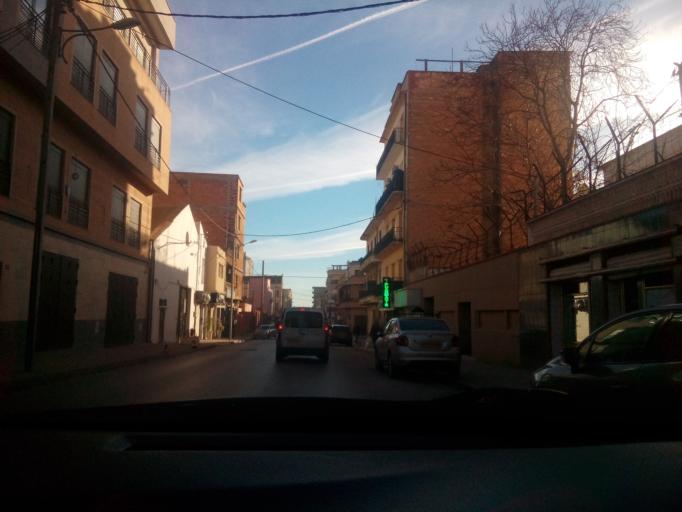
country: DZ
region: Oran
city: Oran
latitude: 35.6874
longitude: -0.6600
